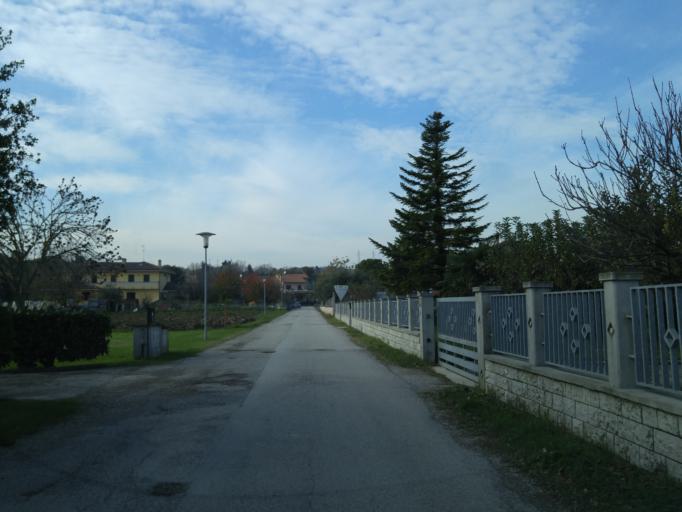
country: IT
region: The Marches
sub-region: Provincia di Pesaro e Urbino
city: Lucrezia
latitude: 43.7813
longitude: 12.9452
